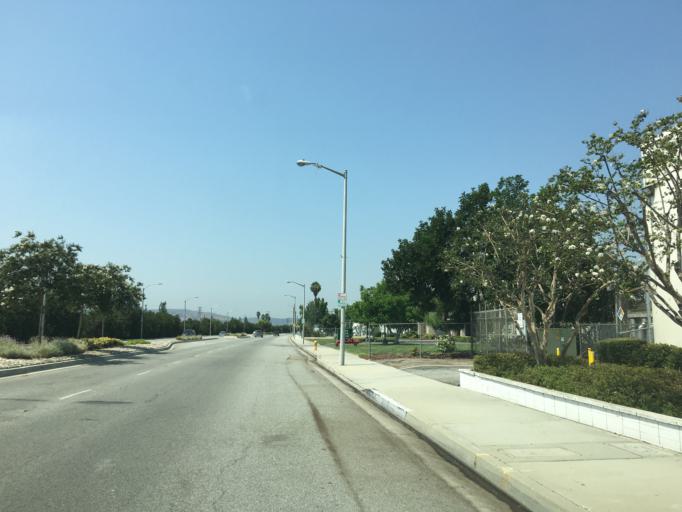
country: US
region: California
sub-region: Los Angeles County
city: Walnut
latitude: 34.0142
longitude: -117.8520
